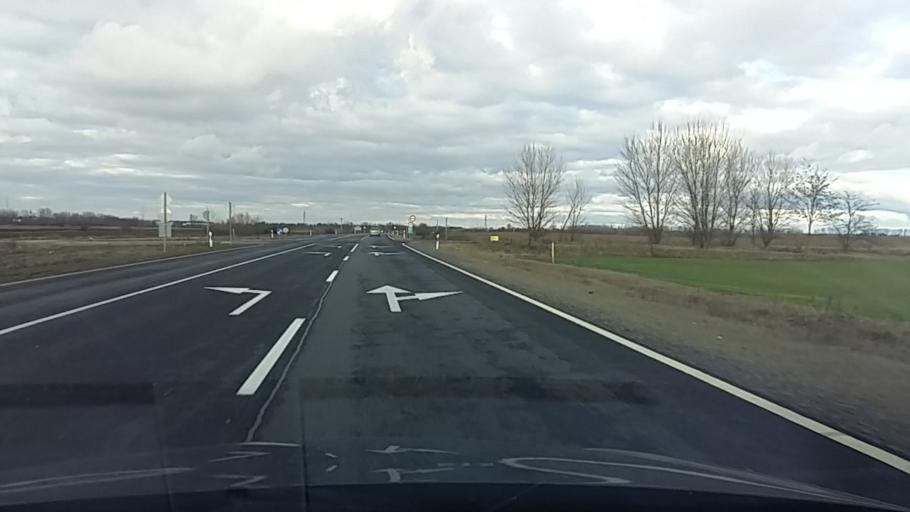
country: HU
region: Szabolcs-Szatmar-Bereg
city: Napkor
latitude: 47.9346
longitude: 21.8188
